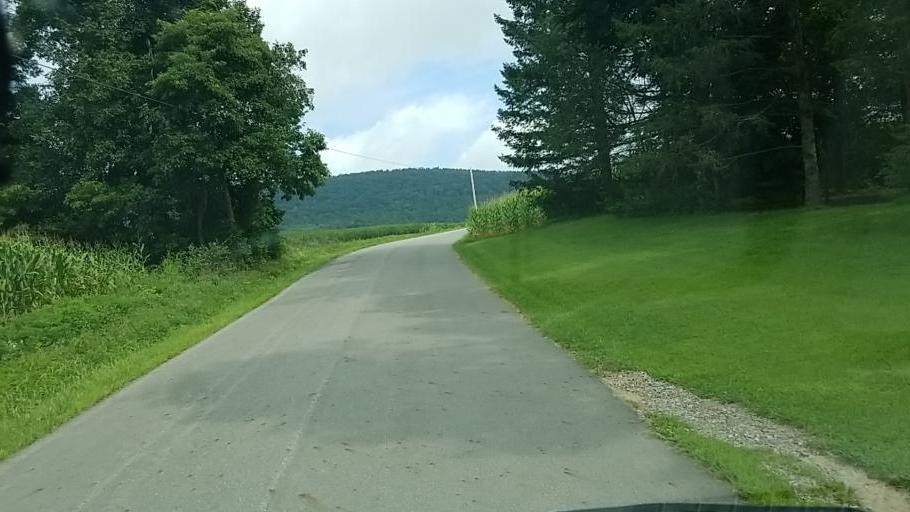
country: US
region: Pennsylvania
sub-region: Dauphin County
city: Millersburg
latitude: 40.5145
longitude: -76.8852
